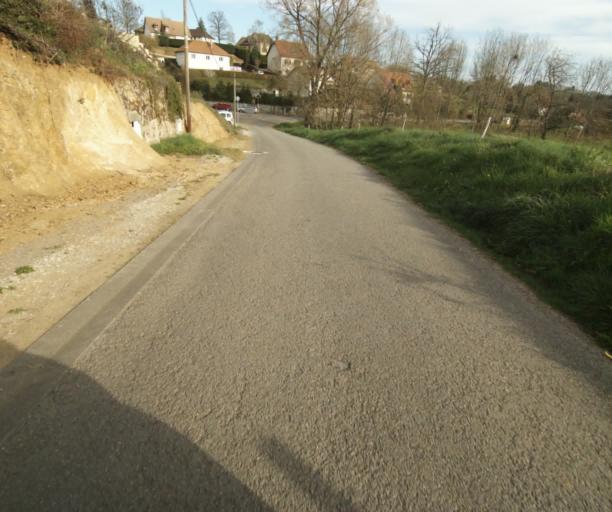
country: FR
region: Limousin
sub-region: Departement de la Correze
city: Naves
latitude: 45.3182
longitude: 1.7574
